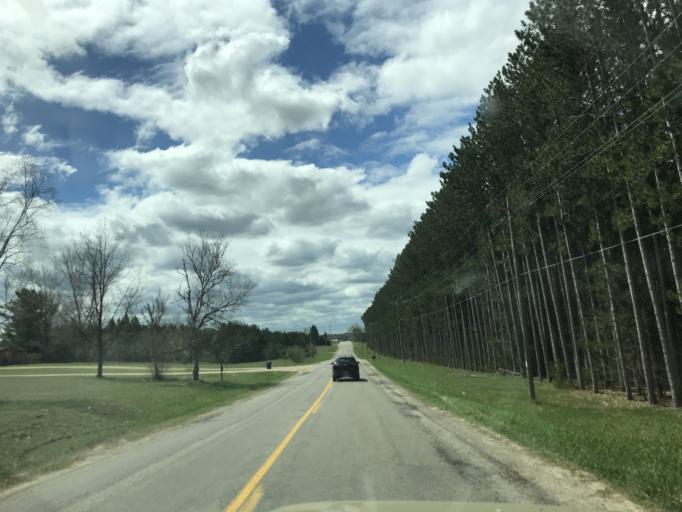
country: US
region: Michigan
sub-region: Otsego County
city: Gaylord
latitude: 45.0385
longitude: -84.6942
